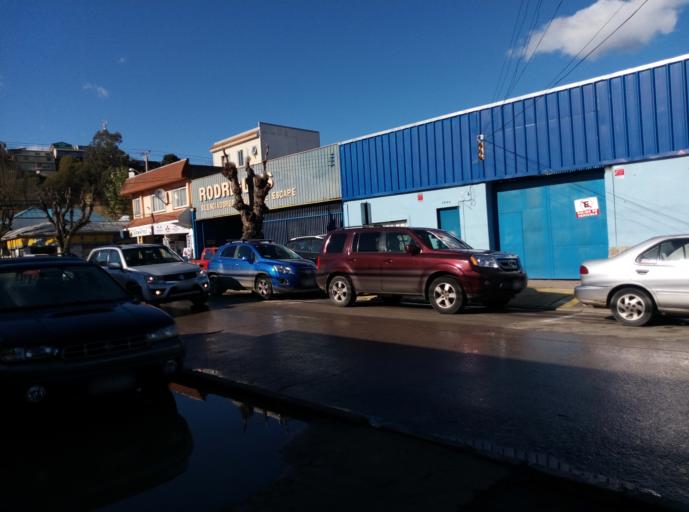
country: CL
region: Valparaiso
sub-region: Provincia de Valparaiso
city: Vina del Mar
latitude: -33.0111
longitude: -71.5424
